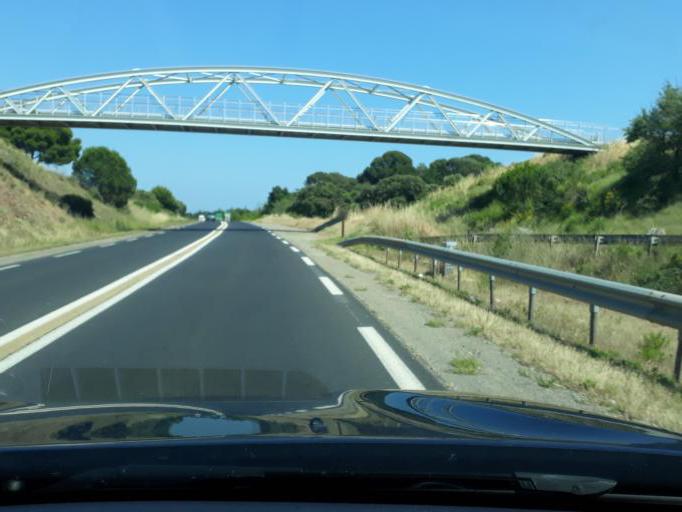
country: FR
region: Languedoc-Roussillon
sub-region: Departement de l'Herault
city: Agde
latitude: 43.2938
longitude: 3.4939
